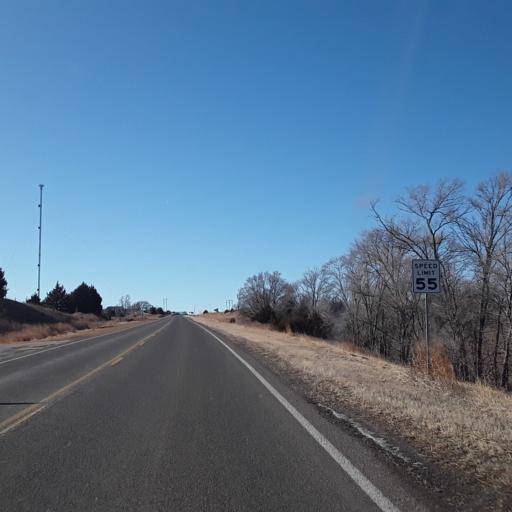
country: US
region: Nebraska
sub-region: Frontier County
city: Stockville
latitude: 40.6576
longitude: -100.6302
